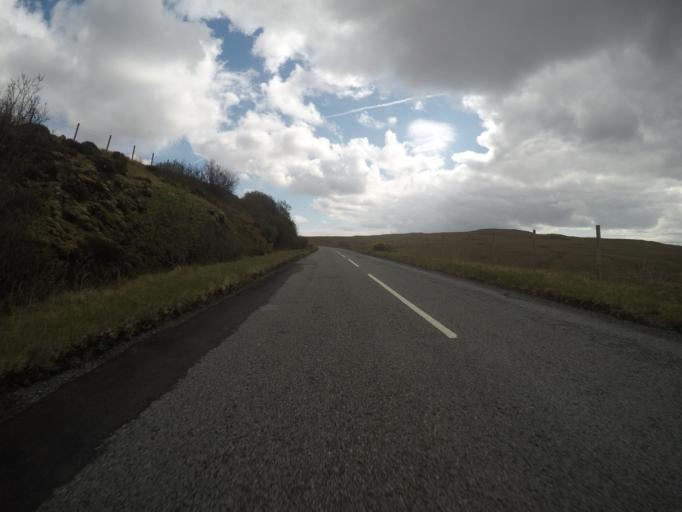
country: GB
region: Scotland
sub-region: Highland
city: Isle of Skye
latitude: 57.3273
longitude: -6.3334
